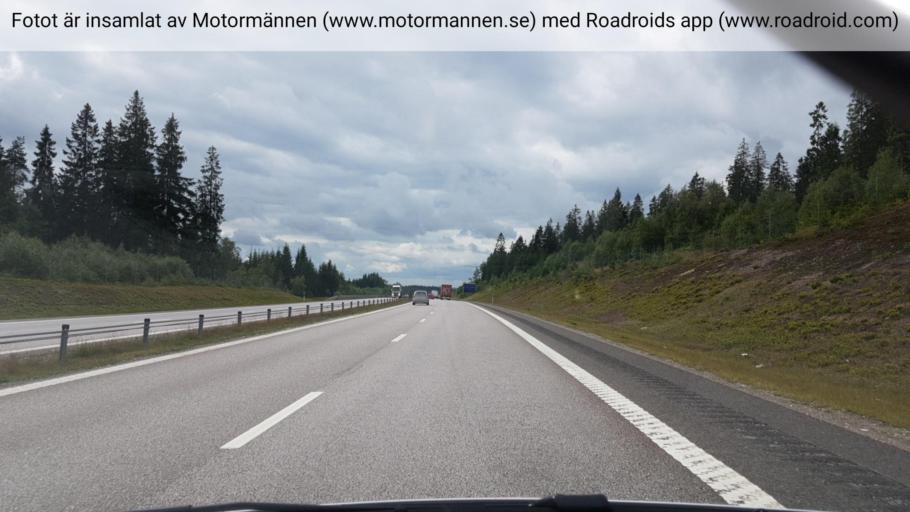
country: SE
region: Vaestra Goetaland
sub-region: Boras Kommun
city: Dalsjofors
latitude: 57.7376
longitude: 13.0436
